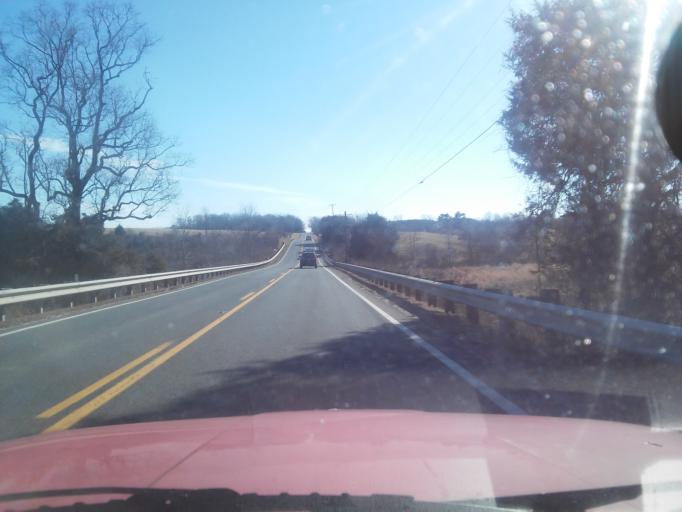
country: US
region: Virginia
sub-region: Orange County
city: Gordonsville
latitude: 38.0207
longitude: -78.1909
